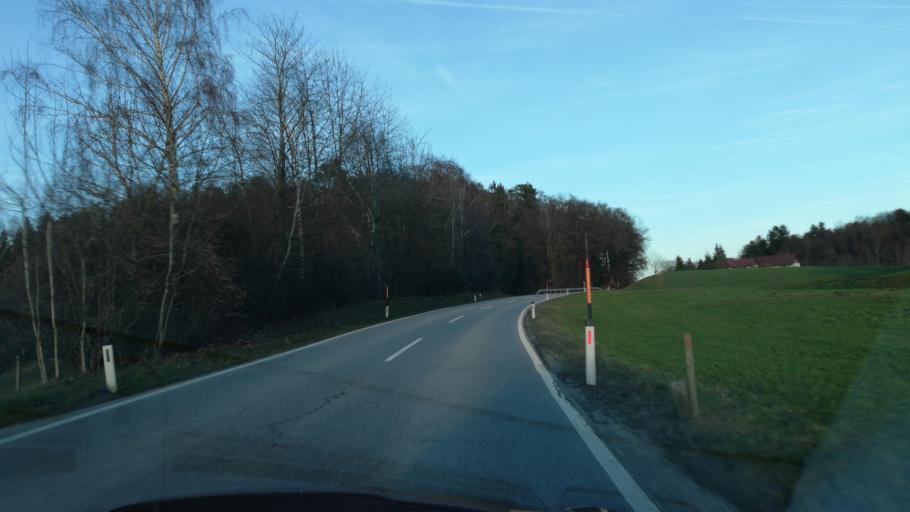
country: AT
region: Salzburg
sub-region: Politischer Bezirk Salzburg-Umgebung
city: Lamprechtshausen
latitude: 48.0807
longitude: 12.9242
